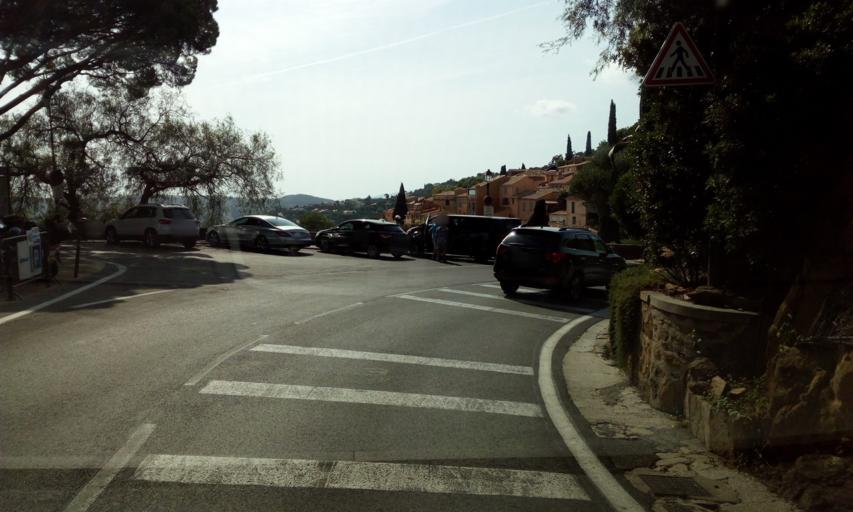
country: FR
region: Provence-Alpes-Cote d'Azur
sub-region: Departement du Var
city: Bormes-les-Mimosas
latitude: 43.1515
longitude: 6.3444
